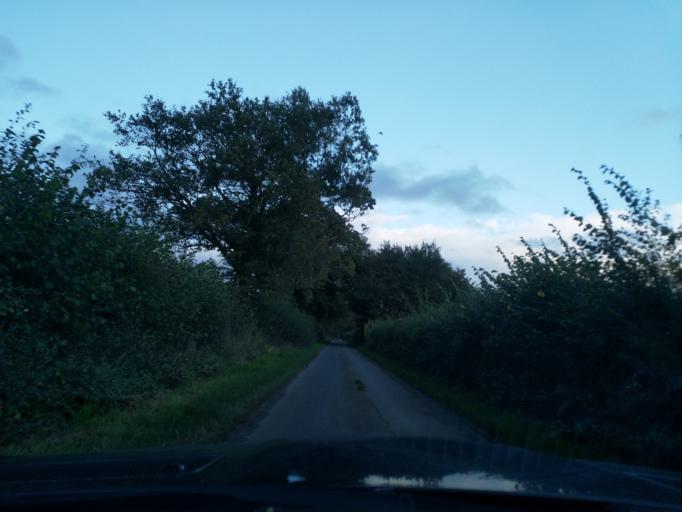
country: GB
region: England
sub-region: Warwickshire
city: Wroxall
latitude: 52.3473
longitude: -1.6596
